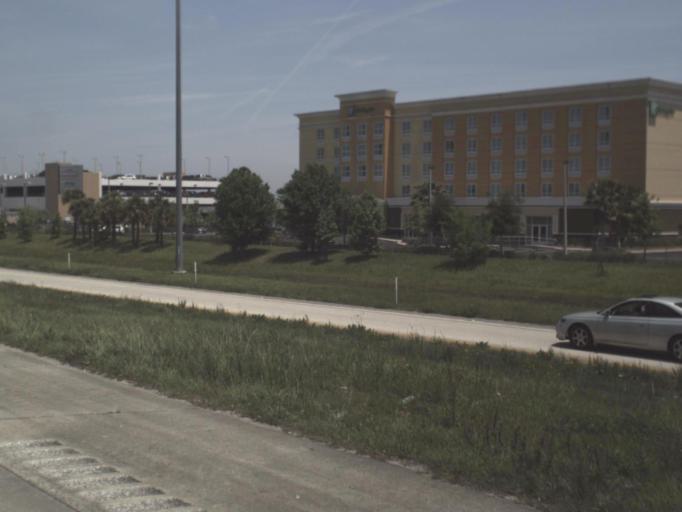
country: US
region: Florida
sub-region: Saint Johns County
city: Ponte Vedra Beach
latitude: 30.2195
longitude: -81.5138
